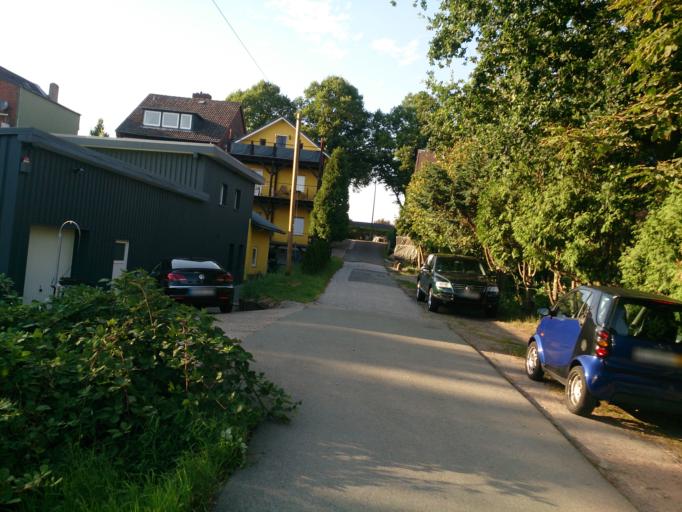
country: DE
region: Hamburg
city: Altona
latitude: 53.5333
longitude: 9.8708
